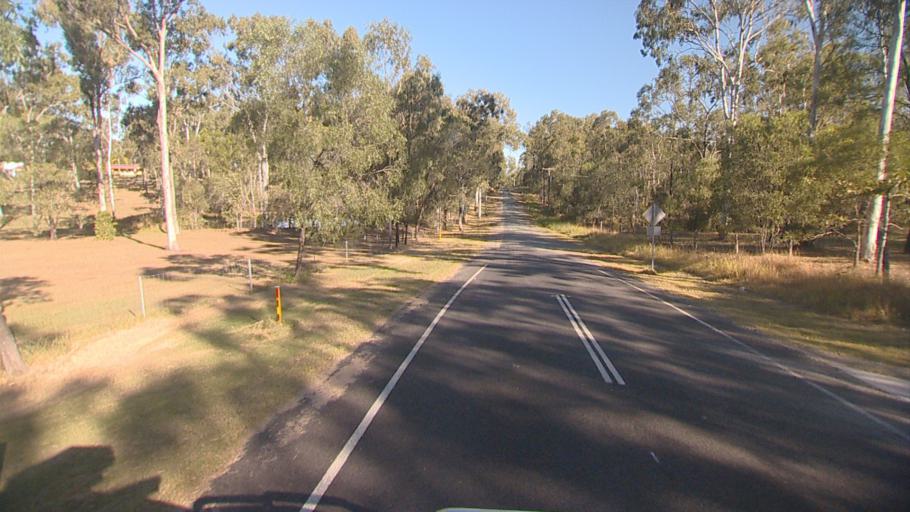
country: AU
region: Queensland
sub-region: Logan
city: North Maclean
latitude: -27.8055
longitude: 153.0341
